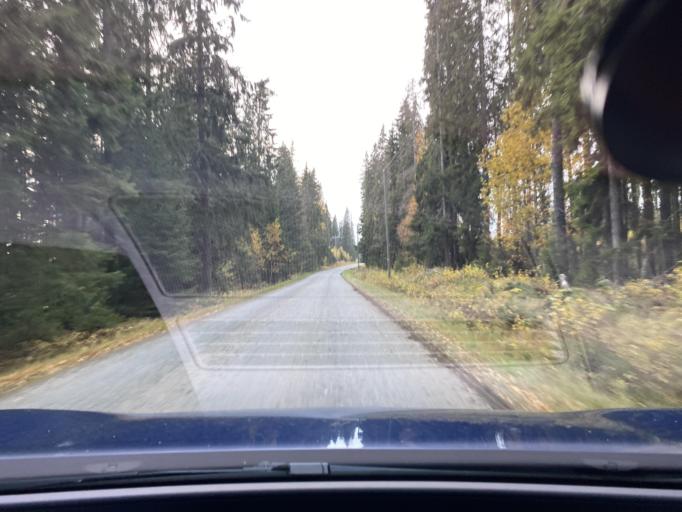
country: FI
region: Varsinais-Suomi
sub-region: Loimaa
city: Alastaro
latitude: 61.0812
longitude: 22.9459
